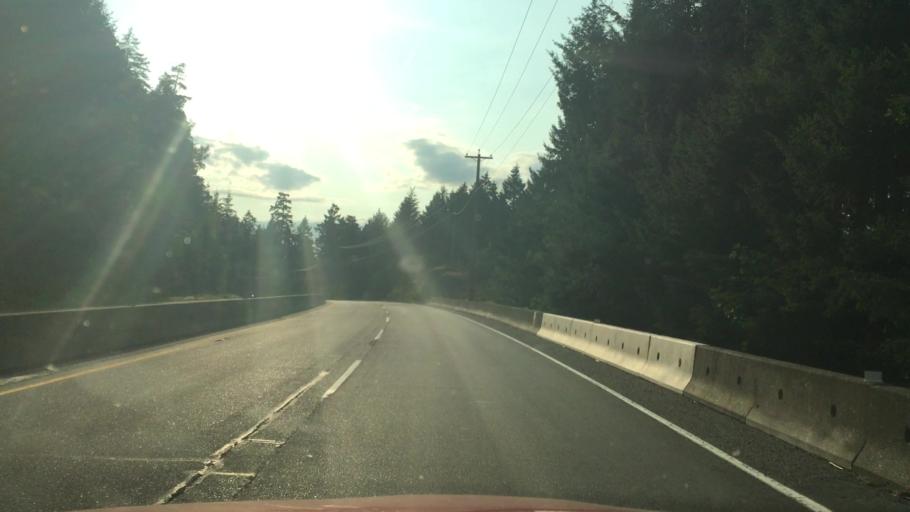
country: CA
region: British Columbia
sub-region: Regional District of Nanaimo
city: Parksville
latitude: 49.3025
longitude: -124.2616
